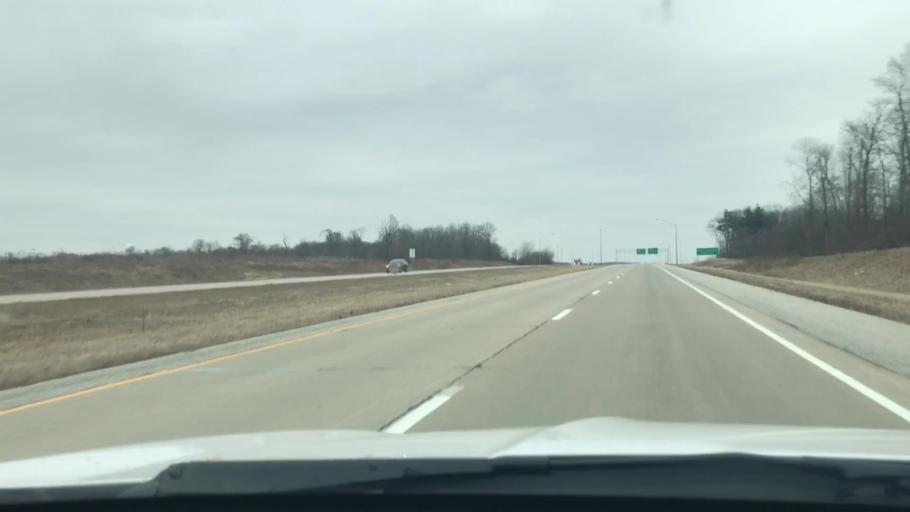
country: US
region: Indiana
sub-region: Miami County
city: Peru
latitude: 40.7709
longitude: -86.1413
